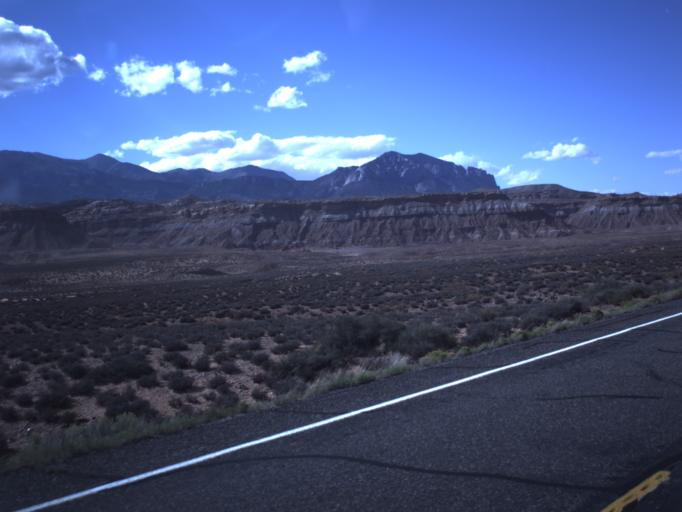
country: US
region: Utah
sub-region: Wayne County
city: Loa
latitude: 38.0808
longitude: -110.6124
